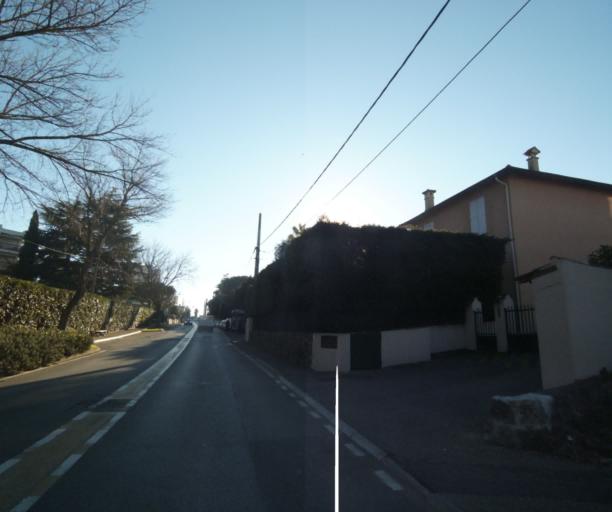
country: FR
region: Provence-Alpes-Cote d'Azur
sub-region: Departement des Alpes-Maritimes
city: Antibes
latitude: 43.5843
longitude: 7.1041
